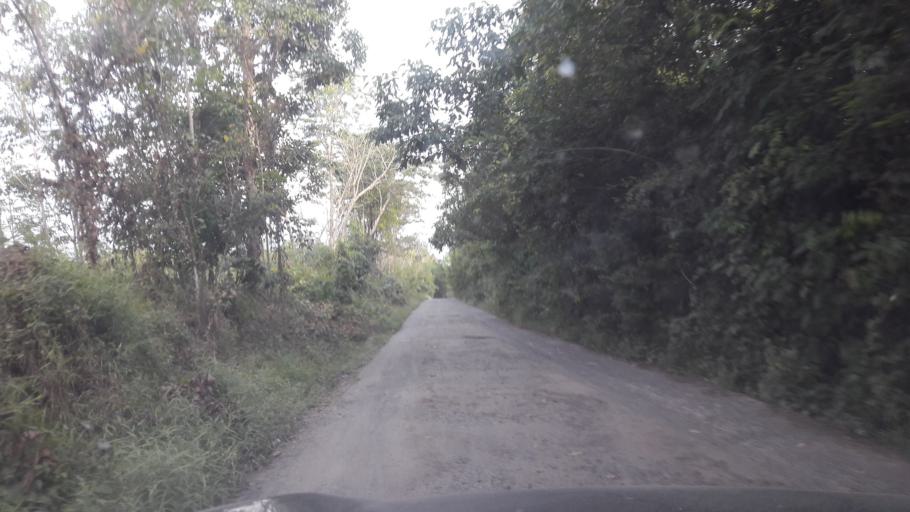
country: ID
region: South Sumatra
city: Gunungmenang
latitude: -3.2733
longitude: 104.0776
